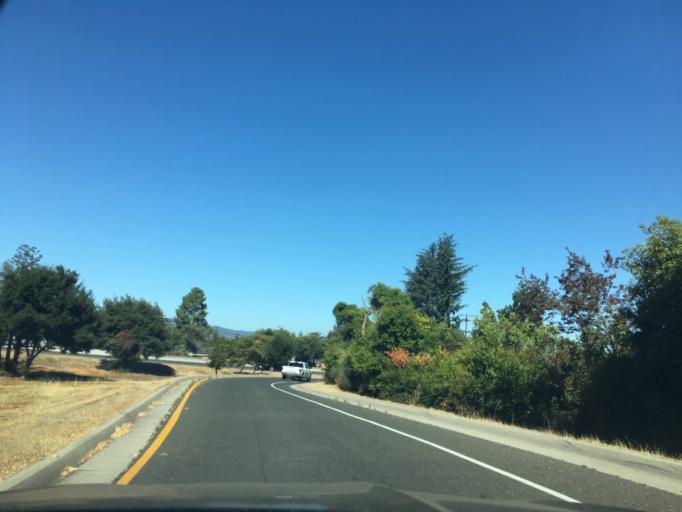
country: US
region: California
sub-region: Santa Clara County
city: Campbell
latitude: 37.2752
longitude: -121.9533
